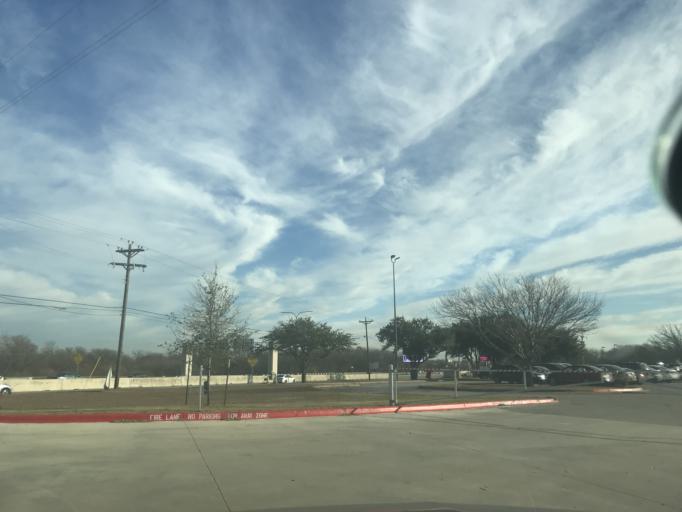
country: US
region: Texas
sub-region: Travis County
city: Manor
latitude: 30.3450
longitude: -97.5742
